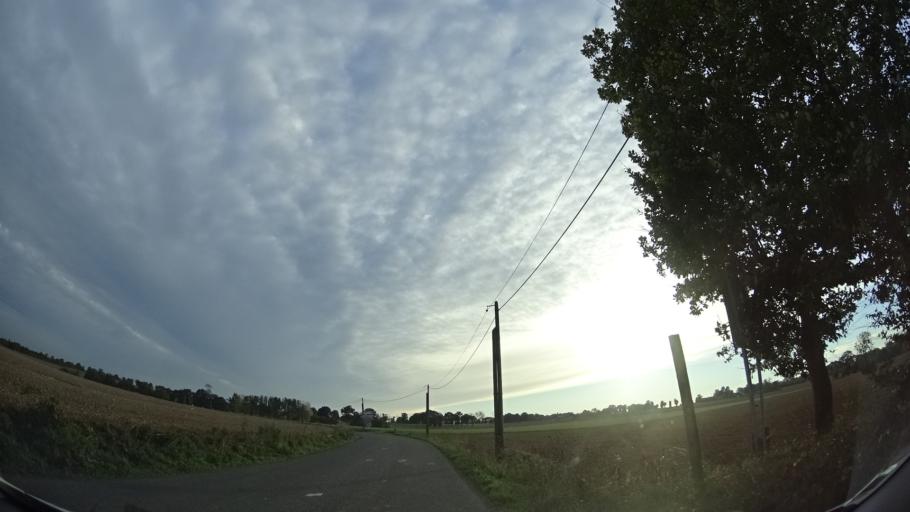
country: FR
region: Brittany
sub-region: Departement d'Ille-et-Vilaine
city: Geveze
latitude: 48.1909
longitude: -1.7935
